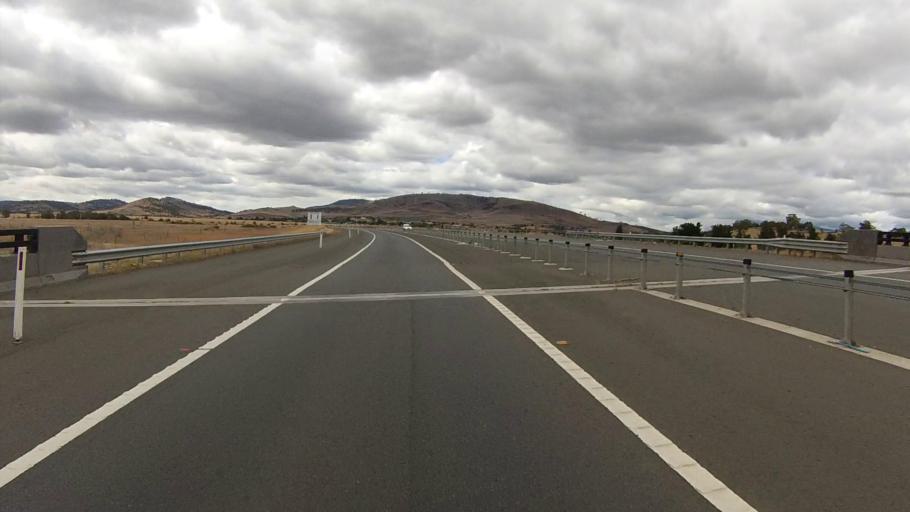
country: AU
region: Tasmania
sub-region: Brighton
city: Bridgewater
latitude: -42.6779
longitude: 147.2720
